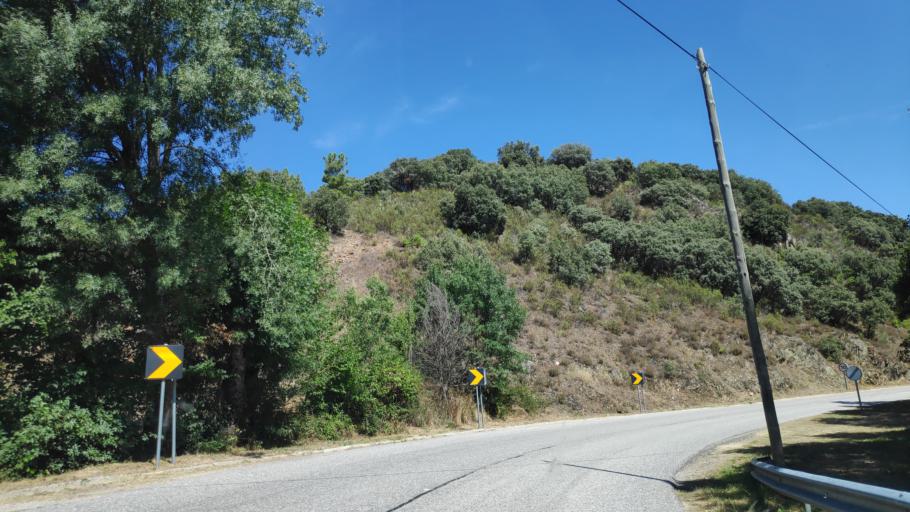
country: PT
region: Braganca
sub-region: Braganca Municipality
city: Braganca
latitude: 41.8602
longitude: -6.7473
